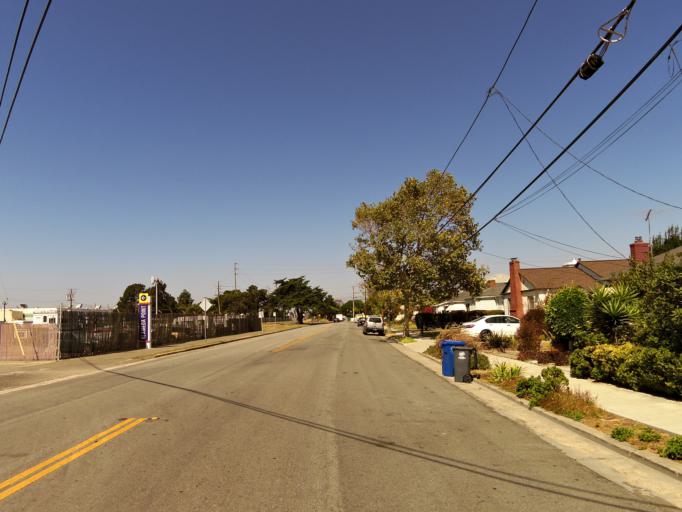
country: US
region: California
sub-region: Alameda County
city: Oakland
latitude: 37.7751
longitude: -122.2911
